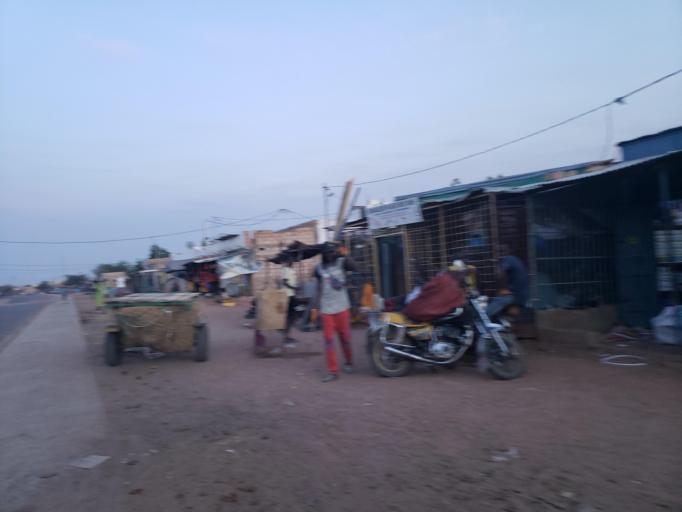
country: SN
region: Matam
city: Ranerou
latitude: 15.2982
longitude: -13.9605
